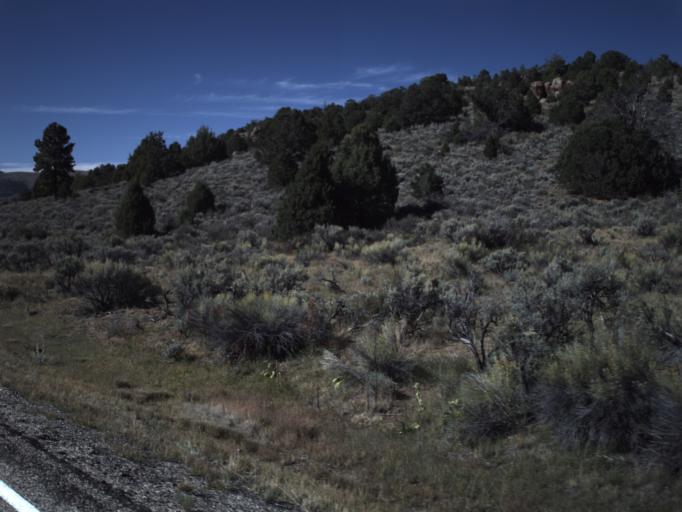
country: US
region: Utah
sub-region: Garfield County
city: Panguitch
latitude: 37.7629
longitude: -112.5279
